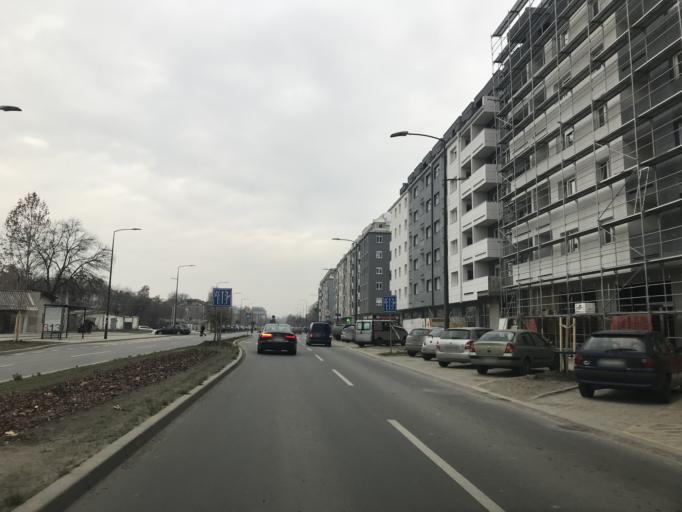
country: RS
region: Autonomna Pokrajina Vojvodina
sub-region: Juznobacki Okrug
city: Novi Sad
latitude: 45.2473
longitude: 19.7998
